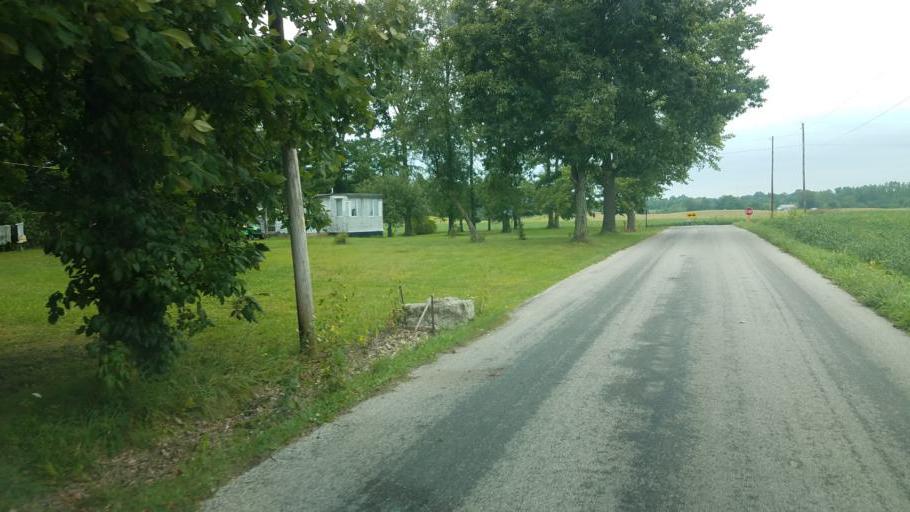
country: US
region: Ohio
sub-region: Morrow County
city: Mount Gilead
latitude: 40.5353
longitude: -82.8018
